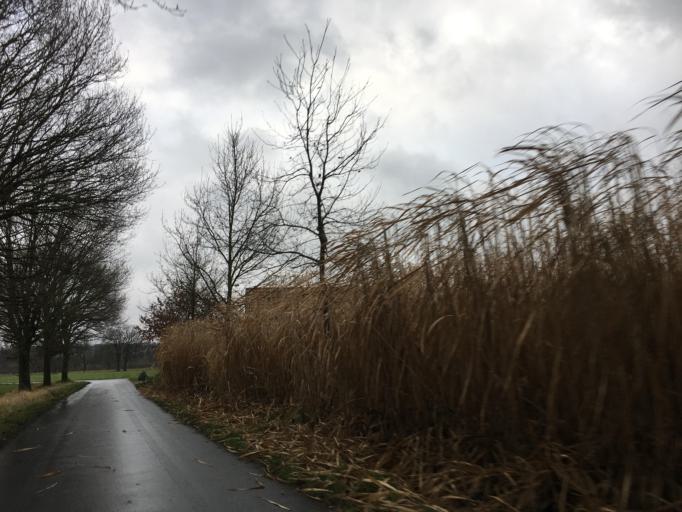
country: DE
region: North Rhine-Westphalia
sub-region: Regierungsbezirk Munster
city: Nordwalde
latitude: 52.1054
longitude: 7.4839
